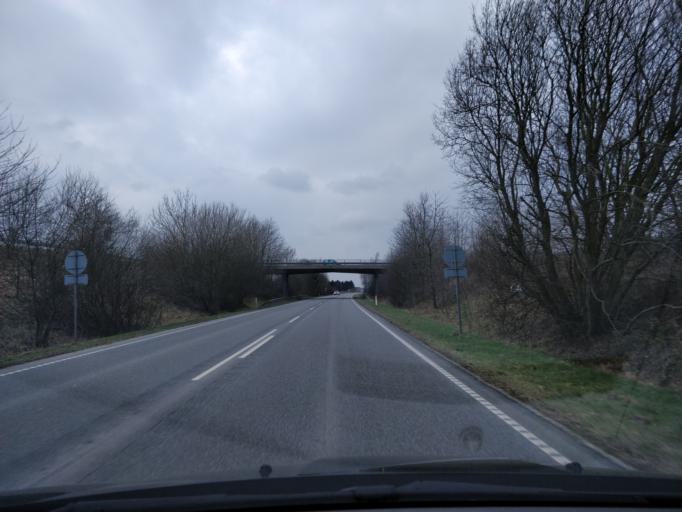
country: DK
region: South Denmark
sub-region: Vejle Kommune
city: Brejning
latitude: 55.6329
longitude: 9.6880
